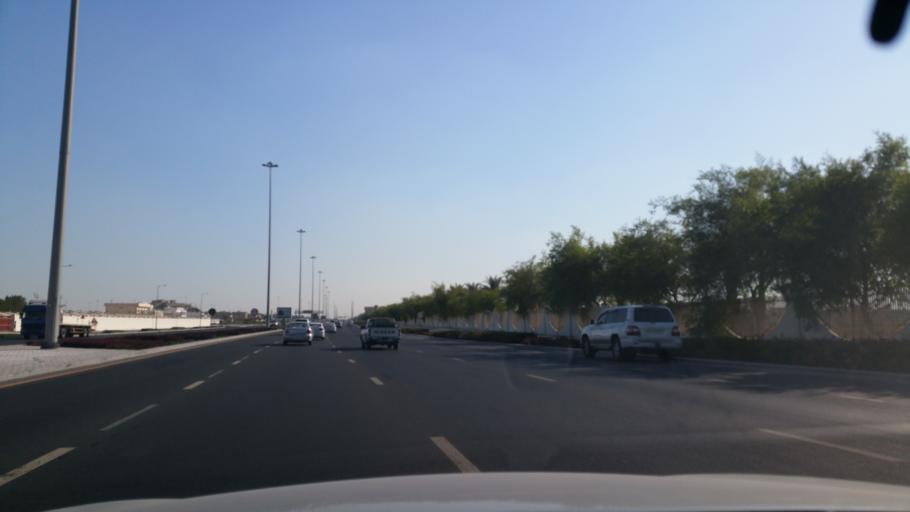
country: QA
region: Baladiyat ar Rayyan
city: Ar Rayyan
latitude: 25.2798
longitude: 51.4311
